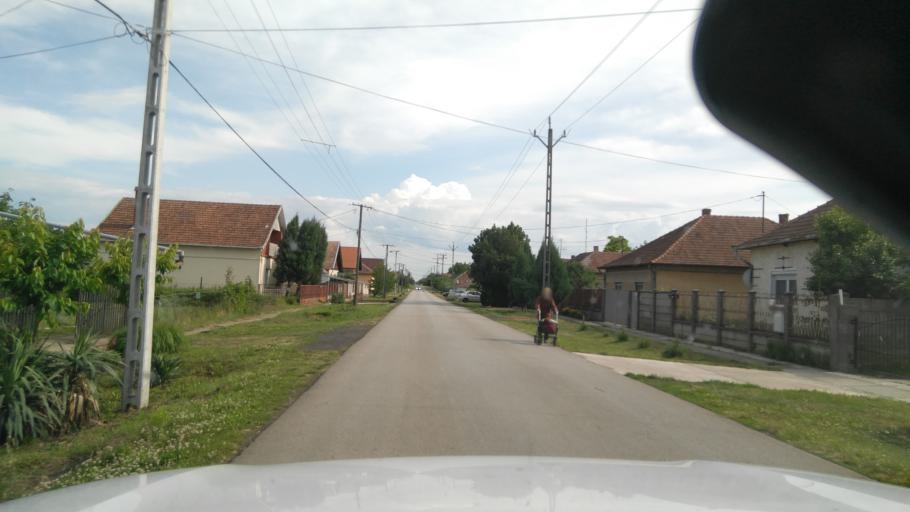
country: HU
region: Bekes
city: Ujkigyos
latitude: 46.5900
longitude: 21.0339
